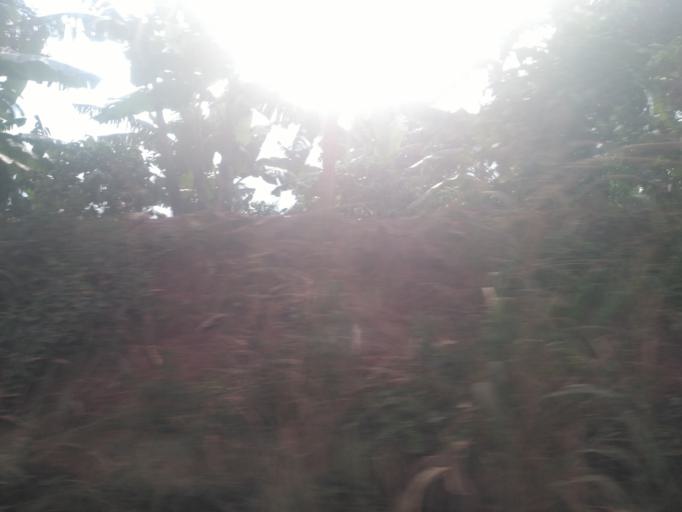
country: UG
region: Central Region
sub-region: Wakiso District
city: Kajansi
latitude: 0.2656
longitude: 32.4375
